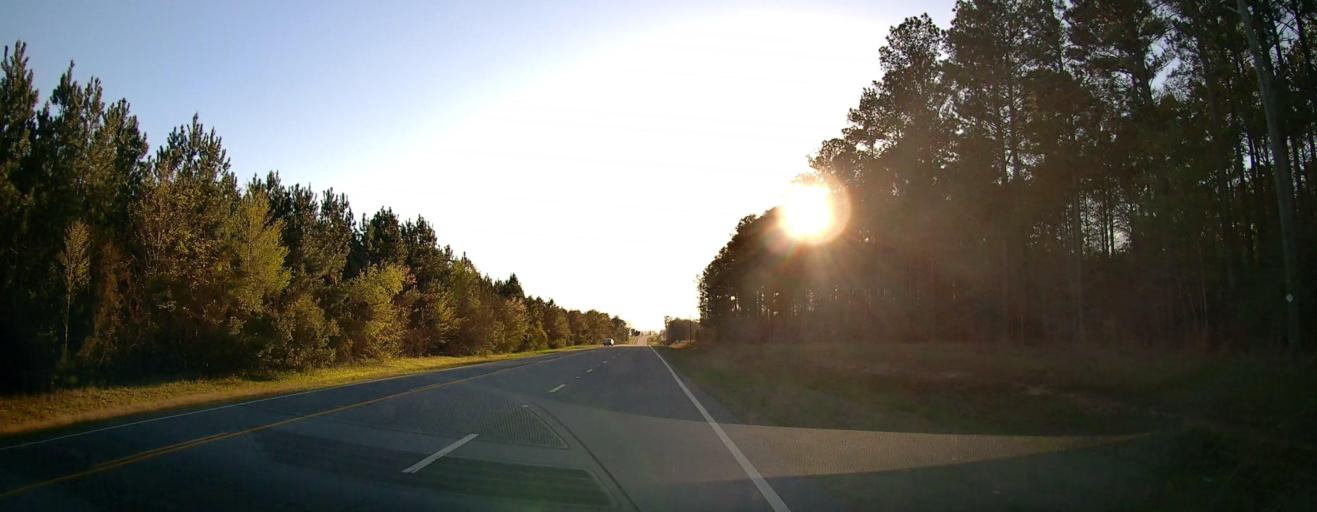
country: US
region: Georgia
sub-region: Wilcox County
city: Rochelle
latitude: 31.9642
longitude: -83.3920
